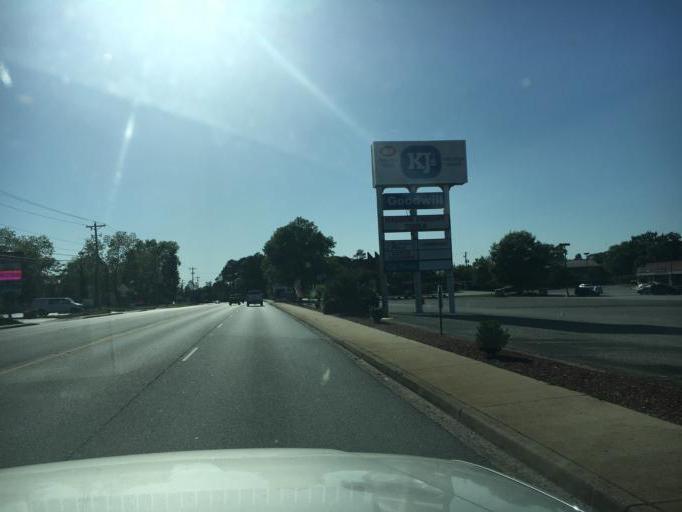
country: US
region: South Carolina
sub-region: Lexington County
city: Saint Andrews
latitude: 34.0453
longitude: -81.1272
